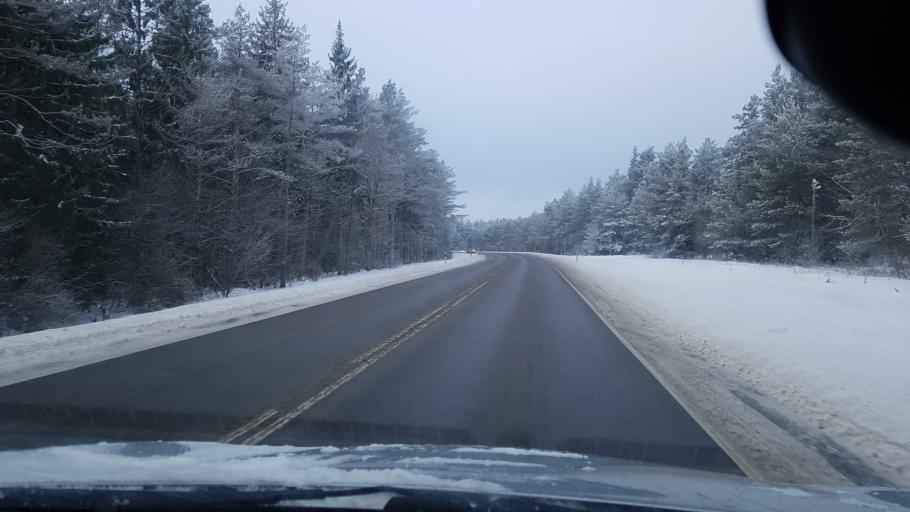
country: EE
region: Harju
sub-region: Keila linn
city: Keila
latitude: 59.3328
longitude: 24.2910
